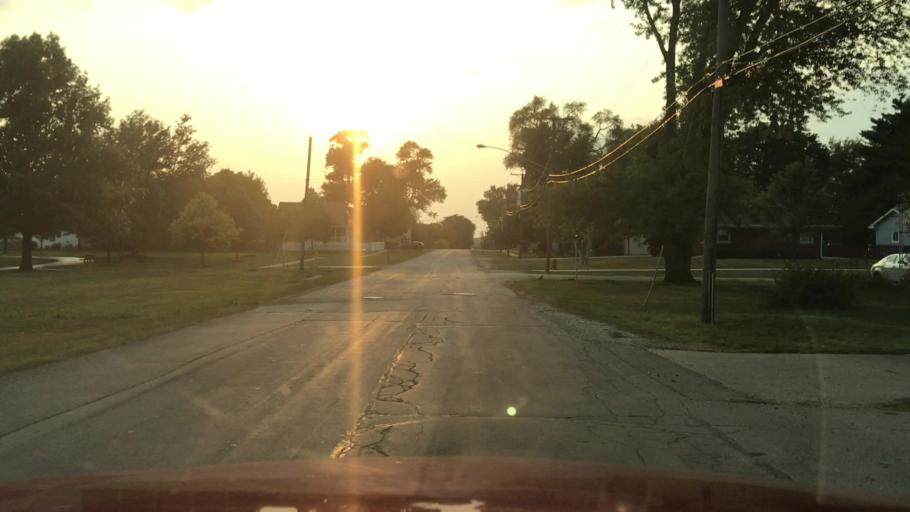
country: US
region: Illinois
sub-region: Will County
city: Lockport
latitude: 41.5783
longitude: -88.0552
